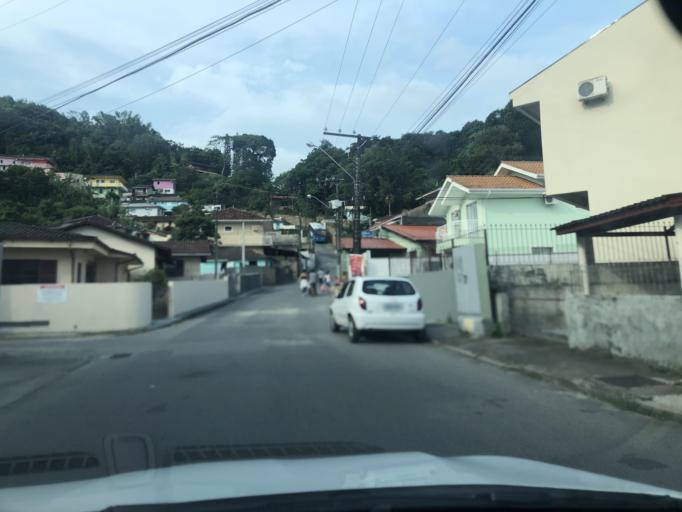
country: BR
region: Santa Catarina
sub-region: Florianopolis
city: Saco dos Limoes
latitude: -27.6028
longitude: -48.5366
